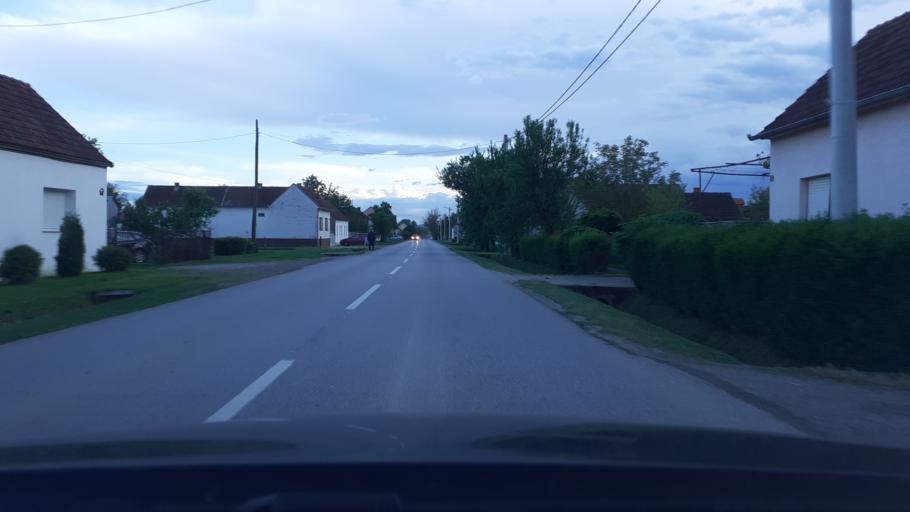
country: HR
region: Pozesko-Slavonska
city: Gradac
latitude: 45.3143
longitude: 17.8126
